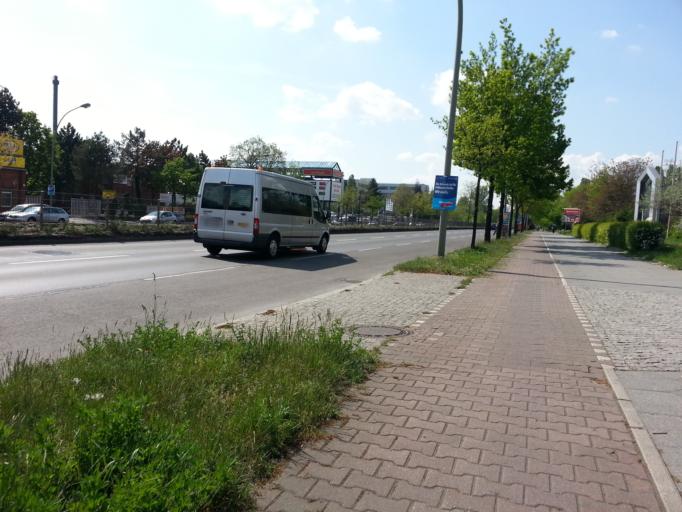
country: DE
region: Berlin
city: Haselhorst
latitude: 52.5386
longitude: 13.2430
